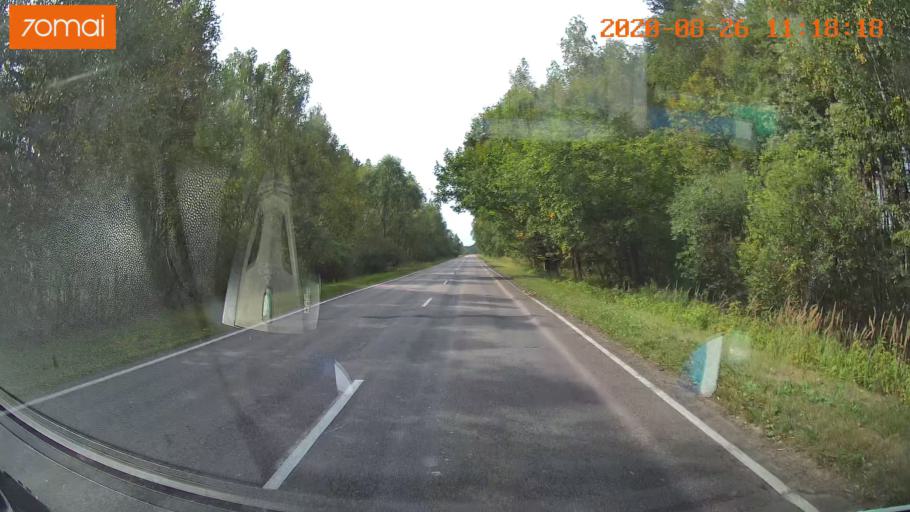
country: RU
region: Rjazan
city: Shilovo
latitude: 54.4113
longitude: 41.0995
